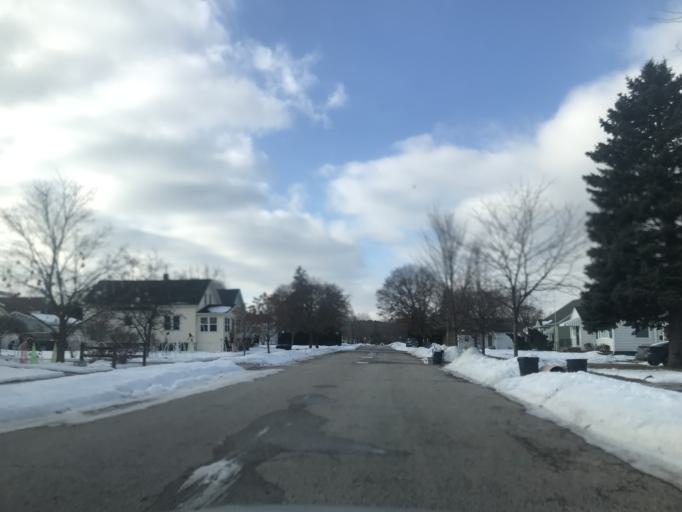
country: US
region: Wisconsin
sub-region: Marinette County
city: Marinette
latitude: 45.1012
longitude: -87.6451
